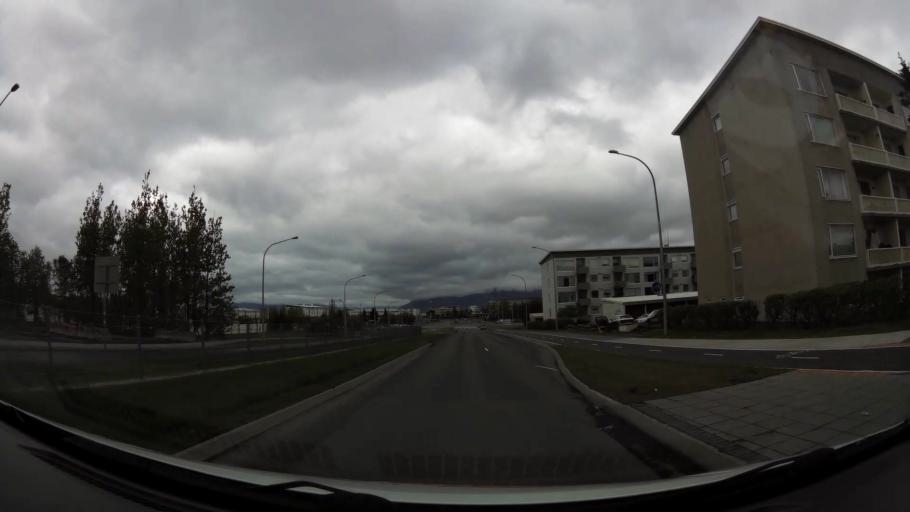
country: IS
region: Capital Region
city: Reykjavik
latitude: 64.1291
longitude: -21.8852
